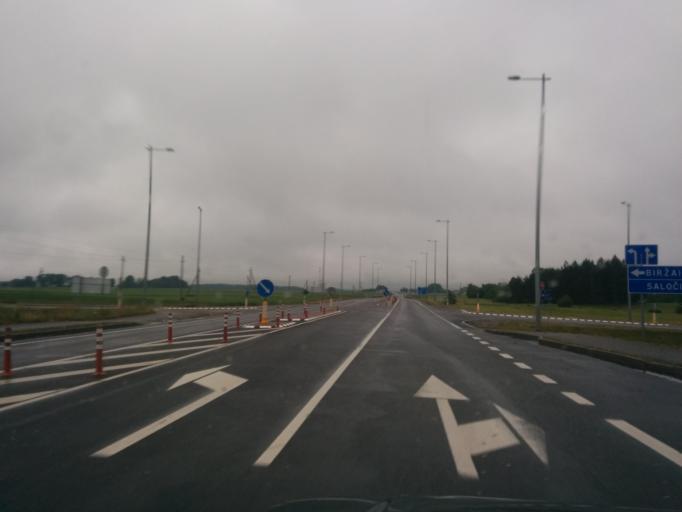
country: LT
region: Panevezys
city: Pasvalys
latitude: 56.2293
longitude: 24.4233
